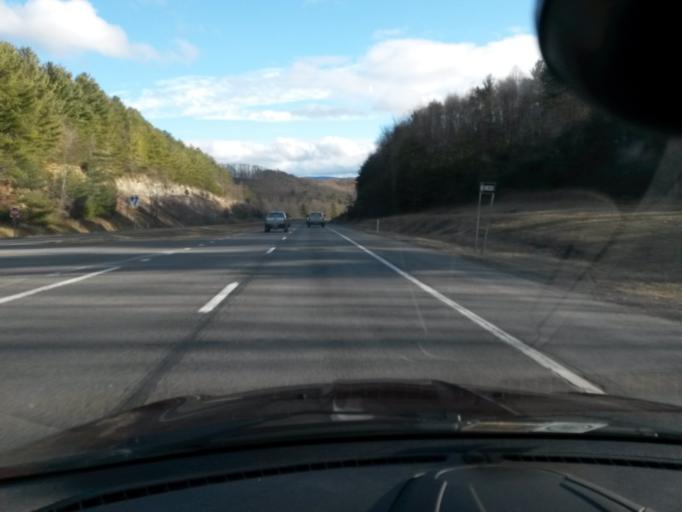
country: US
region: West Virginia
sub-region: Mercer County
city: Athens
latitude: 37.3549
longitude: -81.0200
